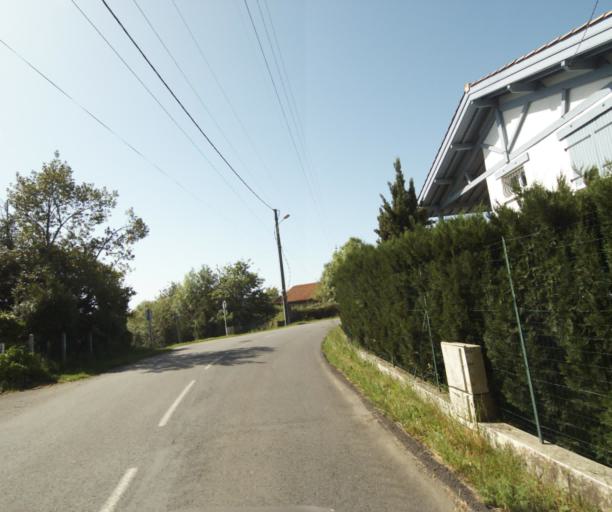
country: FR
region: Aquitaine
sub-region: Departement des Pyrenees-Atlantiques
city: Mouguerre
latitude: 43.4567
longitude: -1.4364
